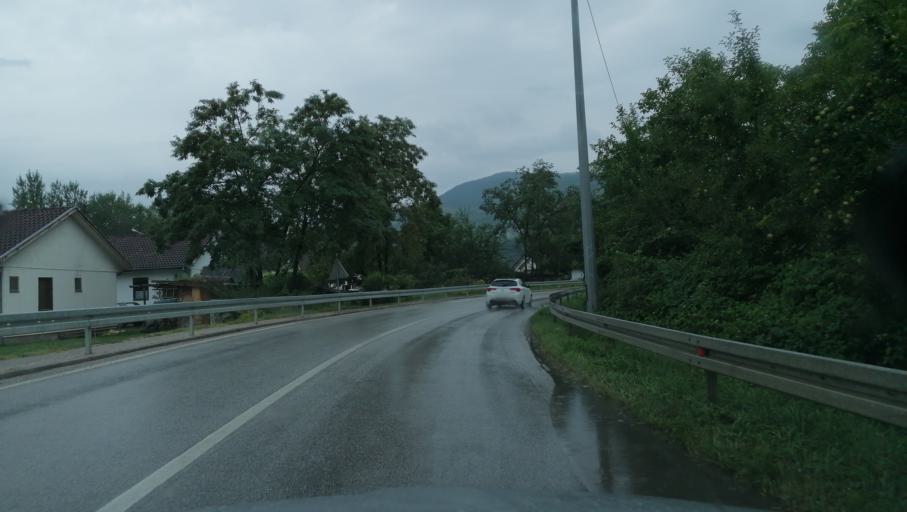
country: BA
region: Federation of Bosnia and Herzegovina
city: Gorazde
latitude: 43.6782
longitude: 19.0152
